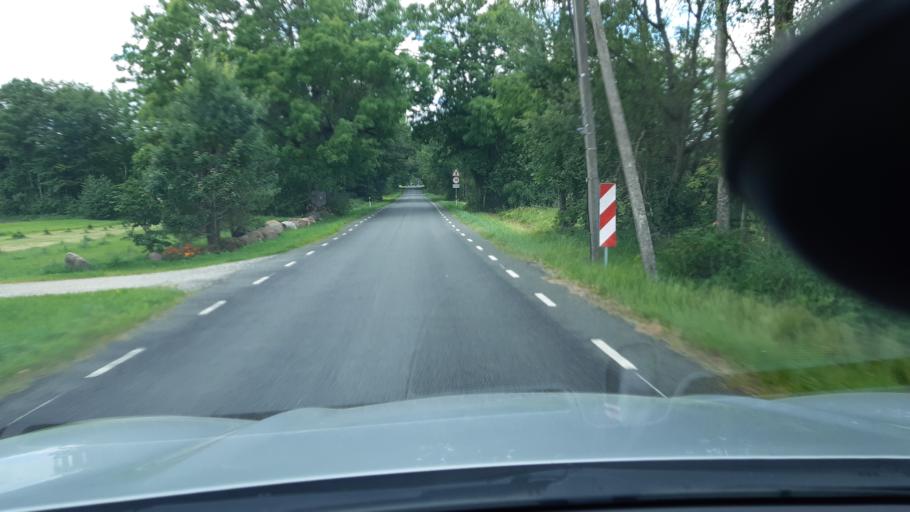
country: EE
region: Raplamaa
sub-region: Jaervakandi vald
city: Jarvakandi
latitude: 58.8745
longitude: 24.7544
